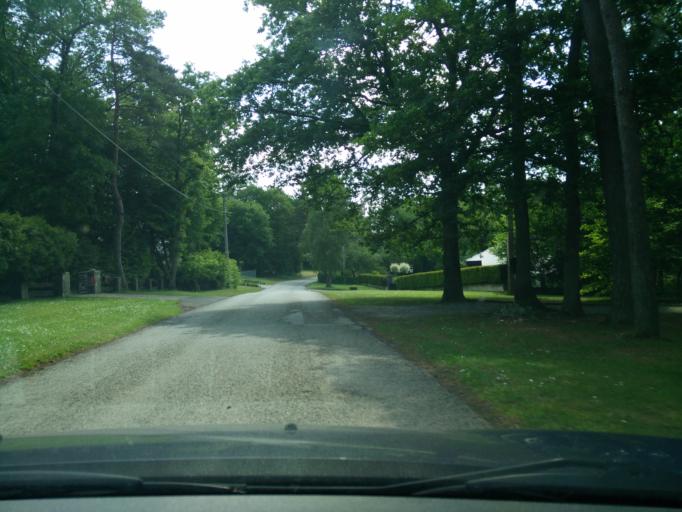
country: BE
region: Wallonia
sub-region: Province de Namur
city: Couvin
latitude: 50.0649
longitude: 4.5228
